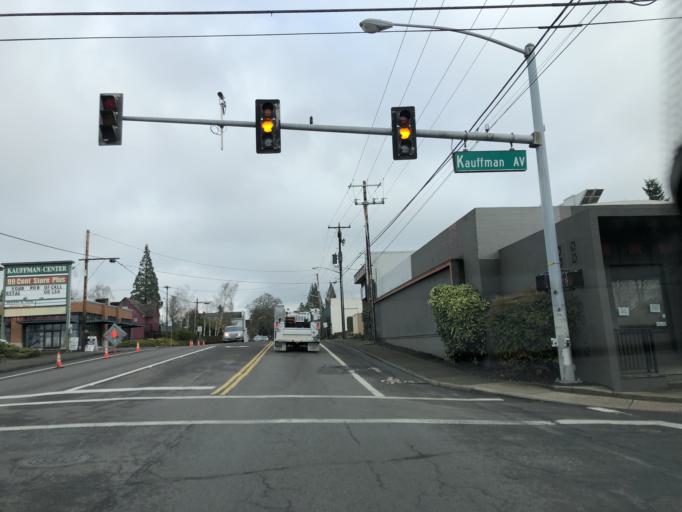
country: US
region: Washington
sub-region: Clark County
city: Vancouver
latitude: 45.6402
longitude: -122.6811
